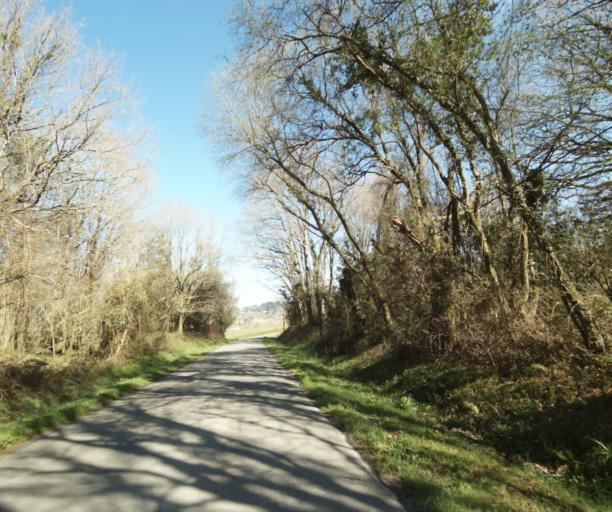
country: FR
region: Aquitaine
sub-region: Departement des Pyrenees-Atlantiques
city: Urrugne
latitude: 43.3645
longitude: -1.6843
